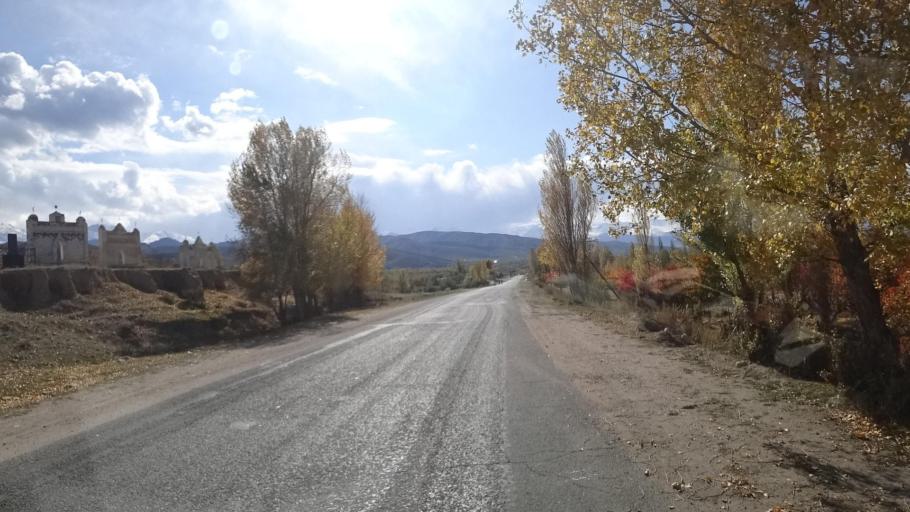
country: KG
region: Ysyk-Koel
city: Pokrovka
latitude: 42.2266
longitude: 77.7135
